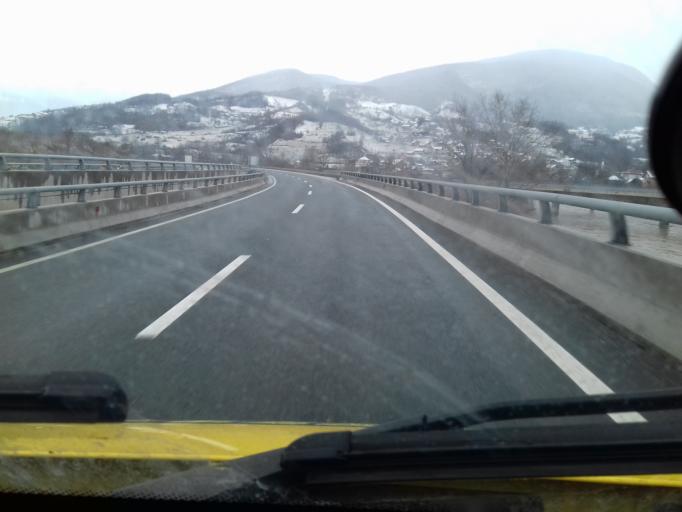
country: BA
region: Federation of Bosnia and Herzegovina
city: Kakanj
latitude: 44.1344
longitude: 18.0823
